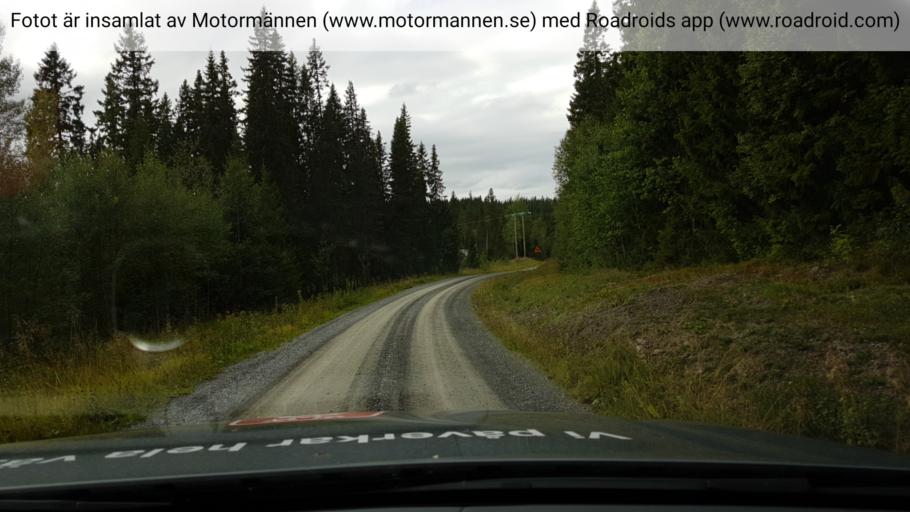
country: SE
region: Jaemtland
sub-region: Krokoms Kommun
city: Valla
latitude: 63.5324
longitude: 13.9127
